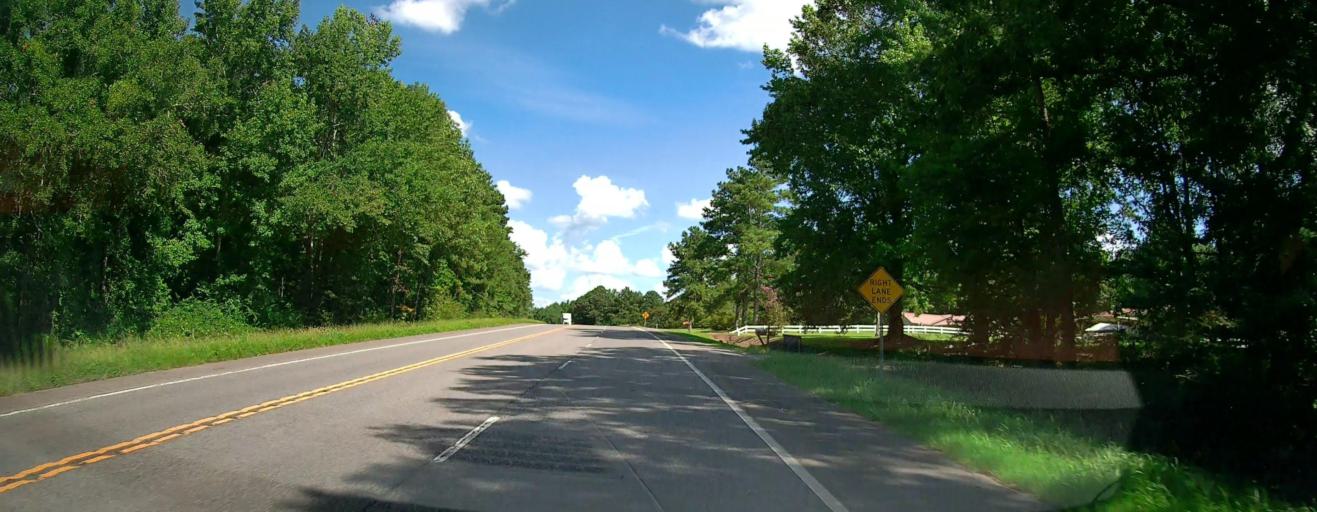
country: US
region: Alabama
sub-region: Pickens County
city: Gordo
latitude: 33.2913
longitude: -87.8713
